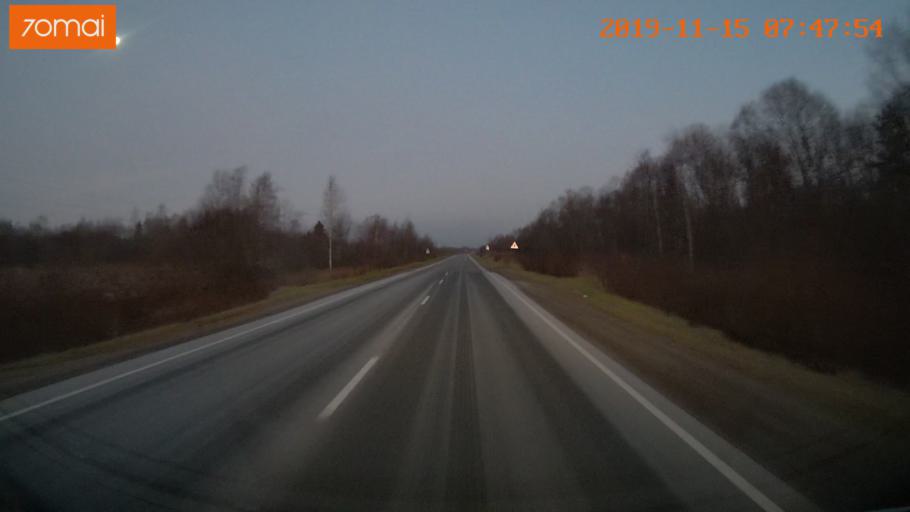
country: RU
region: Vologda
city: Sheksna
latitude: 58.8458
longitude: 38.2527
